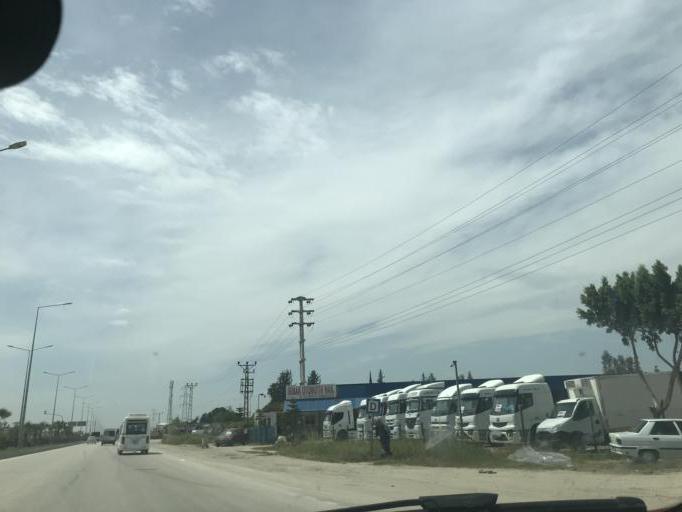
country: TR
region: Adana
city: Yuregir
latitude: 36.9824
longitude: 35.4290
